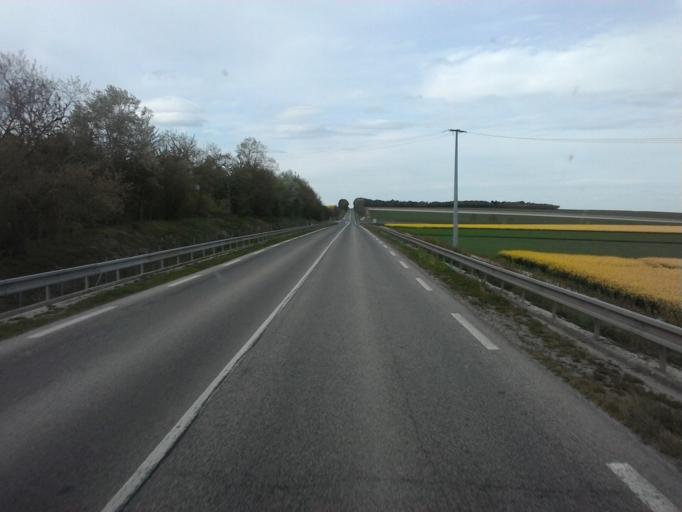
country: FR
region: Champagne-Ardenne
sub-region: Departement de la Marne
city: Compertrix
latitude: 48.8839
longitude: 4.2908
